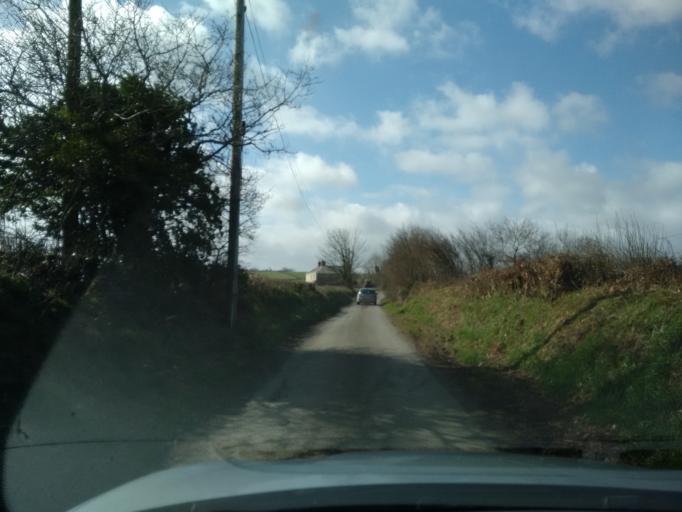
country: GB
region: England
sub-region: Cornwall
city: South Hill
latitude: 50.5763
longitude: -4.3693
